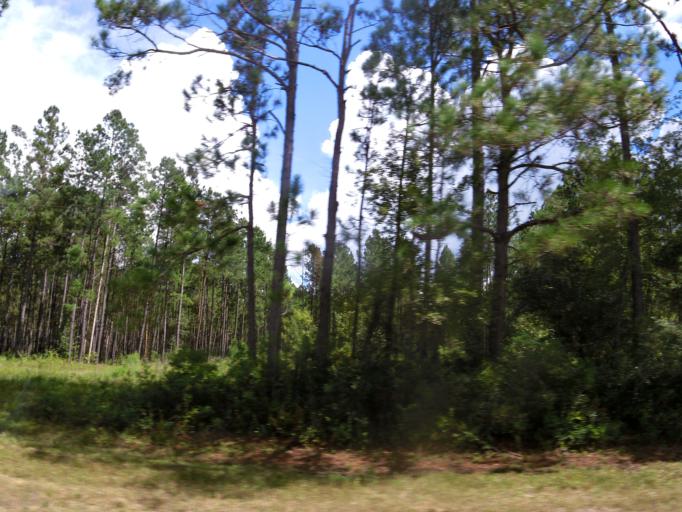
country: US
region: Georgia
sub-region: Charlton County
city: Folkston
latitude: 30.9798
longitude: -82.0252
